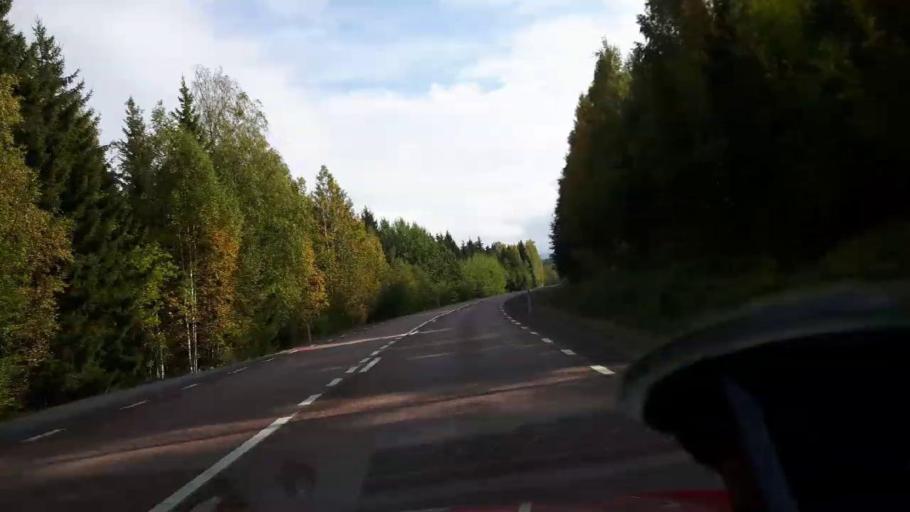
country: SE
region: Gaevleborg
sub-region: Bollnas Kommun
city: Kilafors
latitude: 61.2197
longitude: 16.7144
